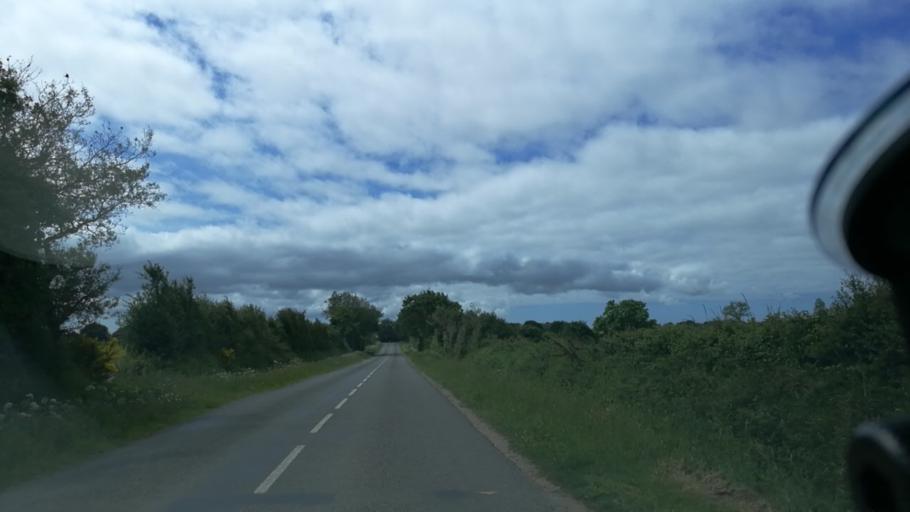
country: FR
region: Brittany
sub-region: Departement du Morbihan
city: Penestin
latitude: 47.4704
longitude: -2.4312
